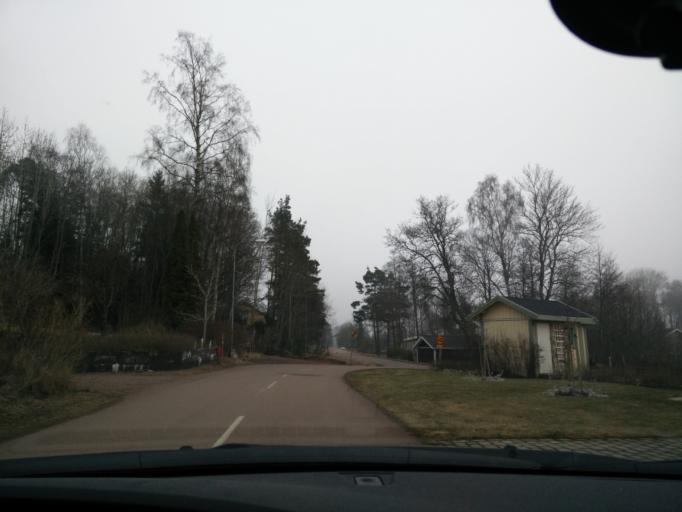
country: AX
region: Mariehamns stad
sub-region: Mariehamn
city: Mariehamn
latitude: 60.1223
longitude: 19.9247
